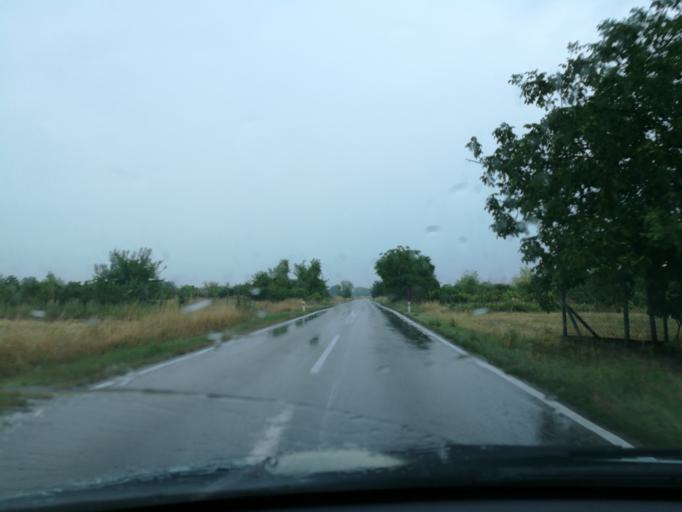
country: HU
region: Komarom-Esztergom
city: Dunaalmas
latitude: 47.7392
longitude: 18.2922
